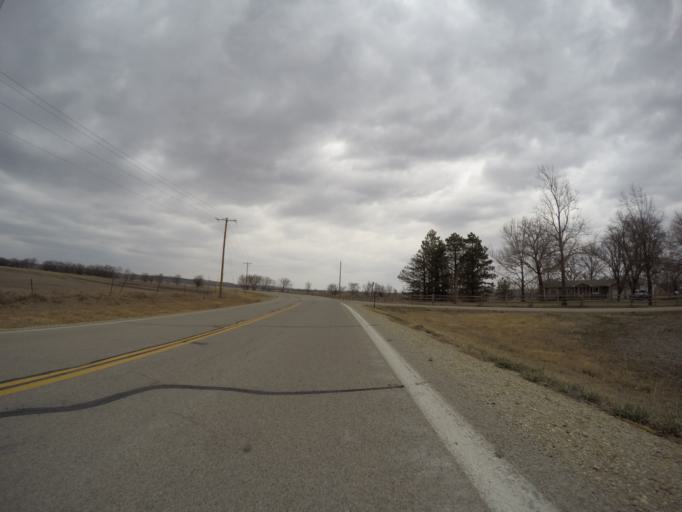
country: US
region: Kansas
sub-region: Riley County
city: Manhattan
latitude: 39.2256
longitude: -96.5585
